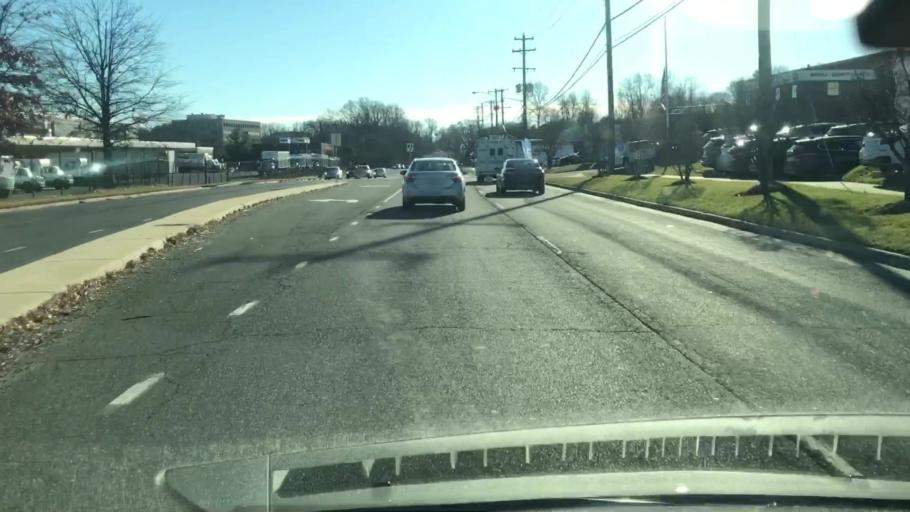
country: US
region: Virginia
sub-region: Fairfax County
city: Merrifield
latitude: 38.8727
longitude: -77.2364
